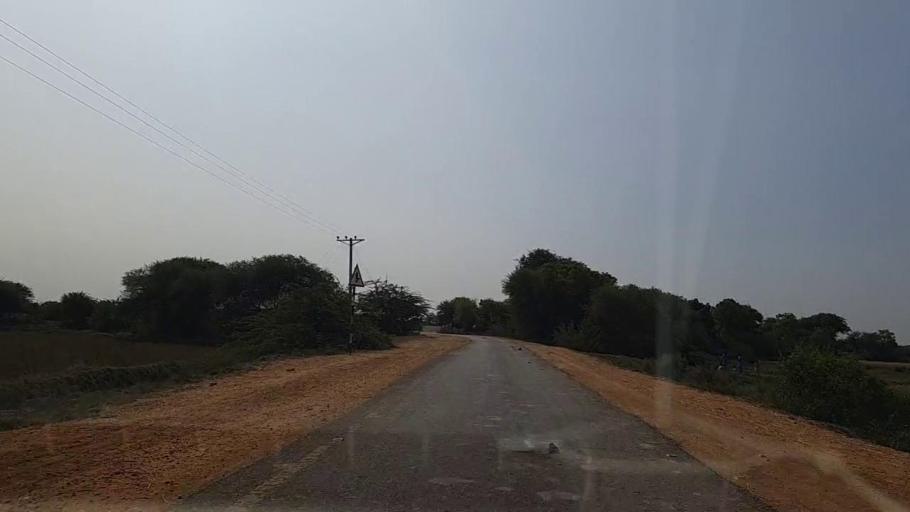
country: PK
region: Sindh
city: Chuhar Jamali
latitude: 24.3473
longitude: 67.9511
